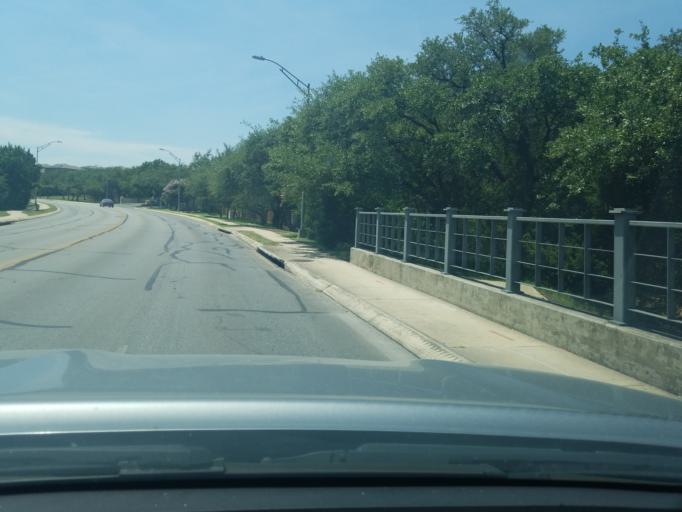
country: US
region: Texas
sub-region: Bexar County
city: Timberwood Park
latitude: 29.6864
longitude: -98.4634
